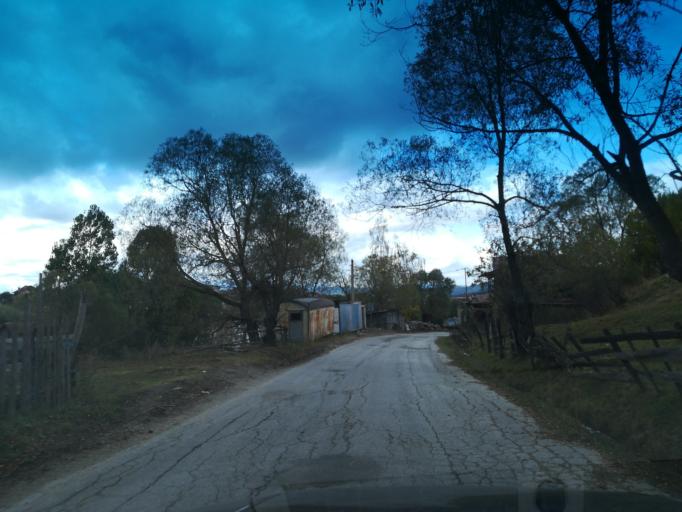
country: BG
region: Pazardzhik
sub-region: Obshtina Batak
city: Batak
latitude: 41.9327
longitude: 24.2708
